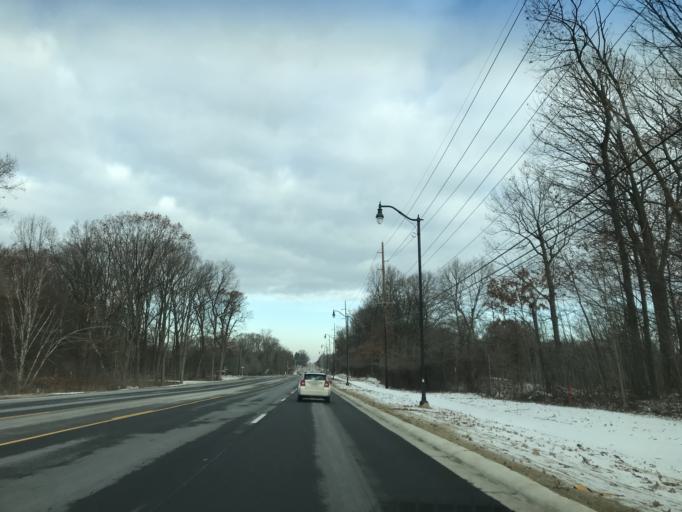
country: US
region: Michigan
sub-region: Oakland County
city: Clarkston
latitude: 42.7450
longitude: -83.3800
